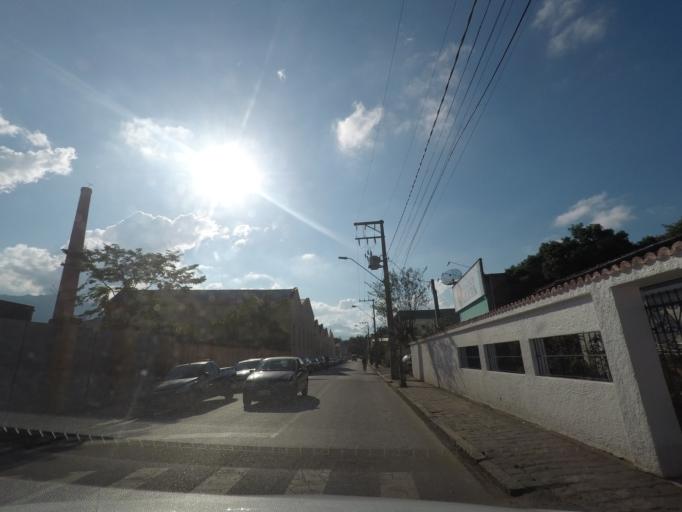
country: BR
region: Parana
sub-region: Antonina
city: Antonina
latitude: -25.4782
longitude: -48.8336
